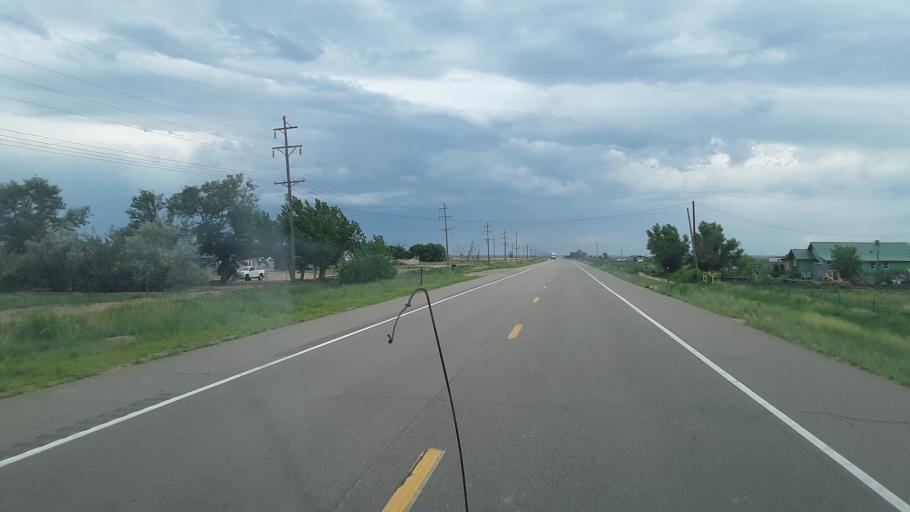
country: US
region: Colorado
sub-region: Crowley County
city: Ordway
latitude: 38.2029
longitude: -103.7482
